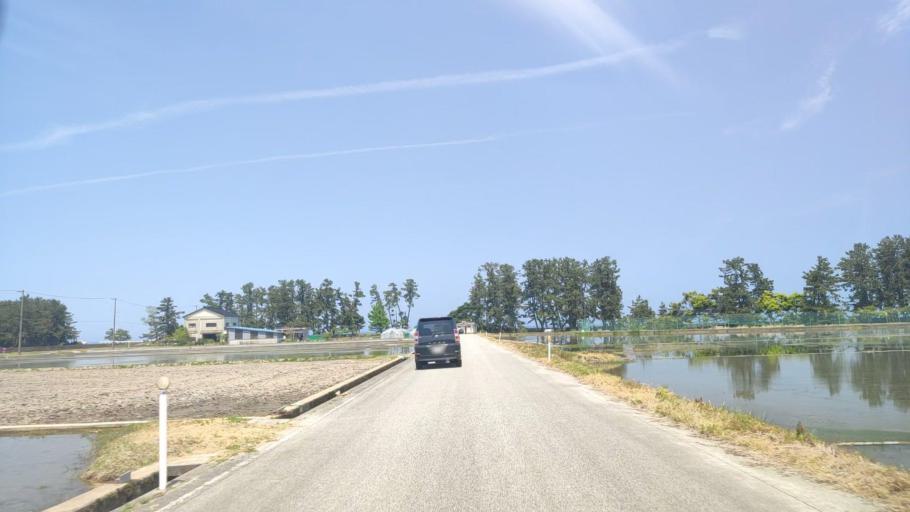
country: JP
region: Toyama
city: Nyuzen
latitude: 36.9611
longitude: 137.5676
